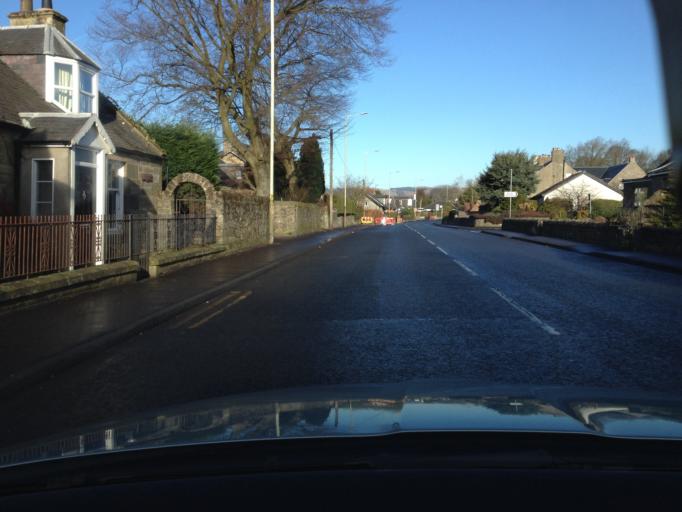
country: GB
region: Scotland
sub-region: Perth and Kinross
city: Kinross
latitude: 56.2128
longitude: -3.4265
